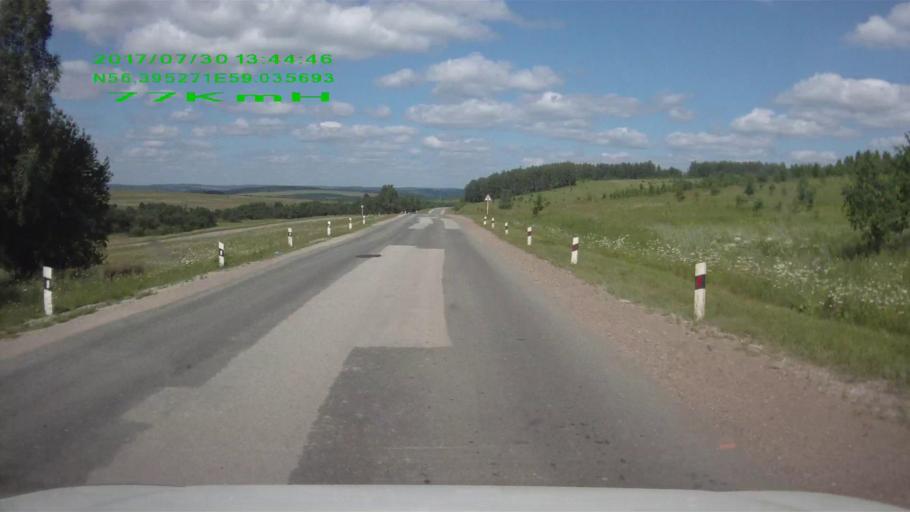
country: RU
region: Sverdlovsk
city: Mikhaylovsk
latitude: 56.3957
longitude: 59.0357
